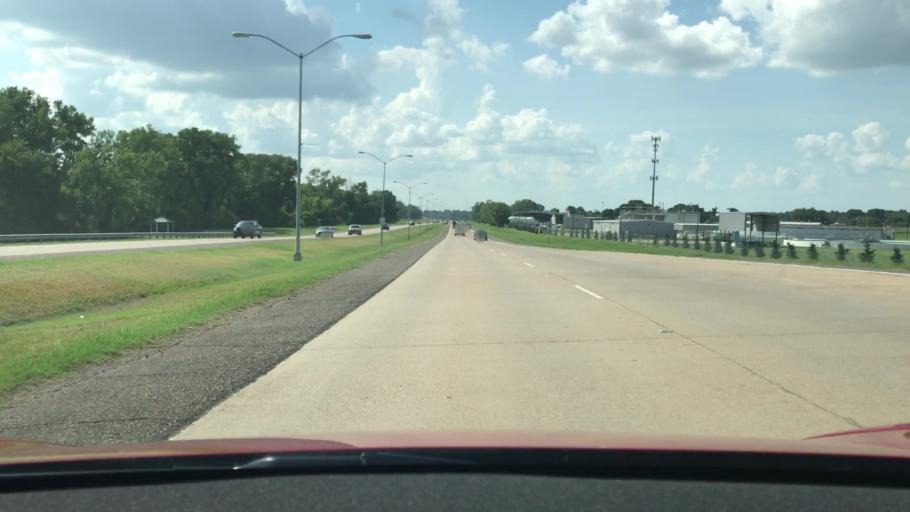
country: US
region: Louisiana
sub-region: Bossier Parish
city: Bossier City
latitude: 32.4789
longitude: -93.6808
